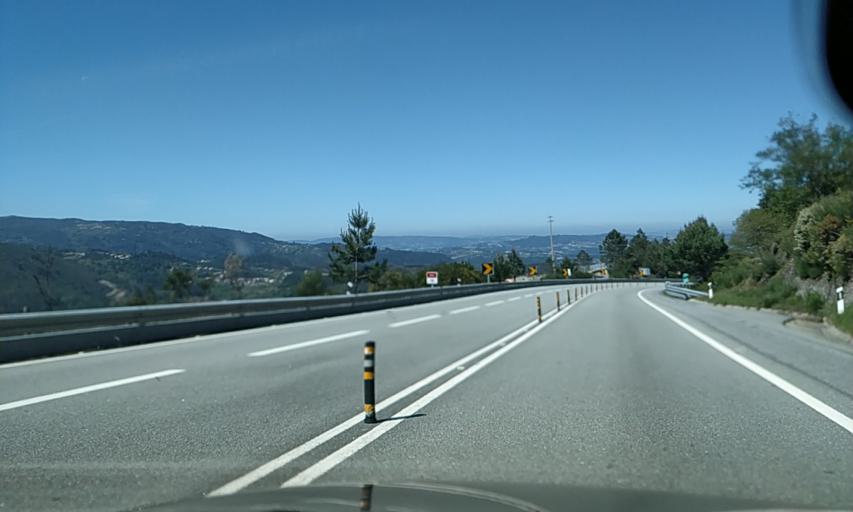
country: PT
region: Porto
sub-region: Baiao
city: Valadares
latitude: 41.2562
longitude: -7.9656
